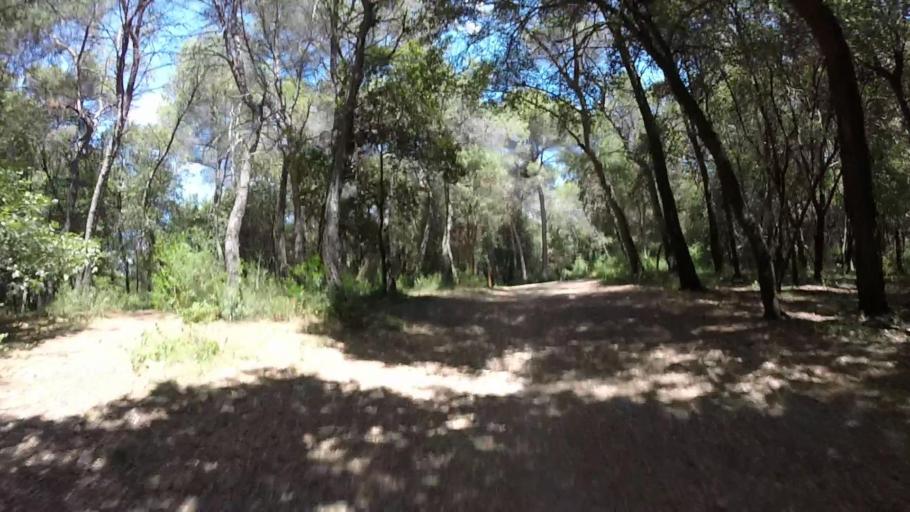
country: FR
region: Provence-Alpes-Cote d'Azur
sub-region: Departement des Alpes-Maritimes
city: Mougins
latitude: 43.6004
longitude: 7.0229
